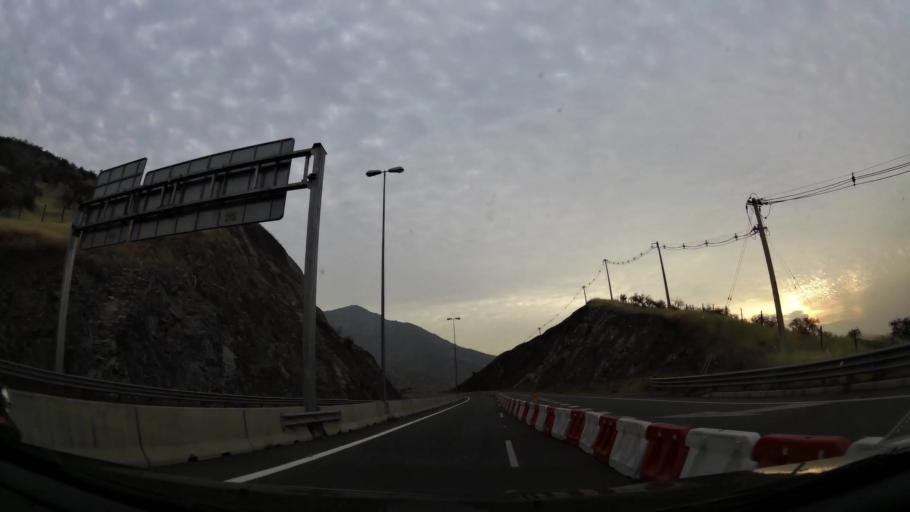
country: CL
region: Santiago Metropolitan
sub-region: Provincia de Chacabuco
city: Chicureo Abajo
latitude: -33.3282
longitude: -70.6260
